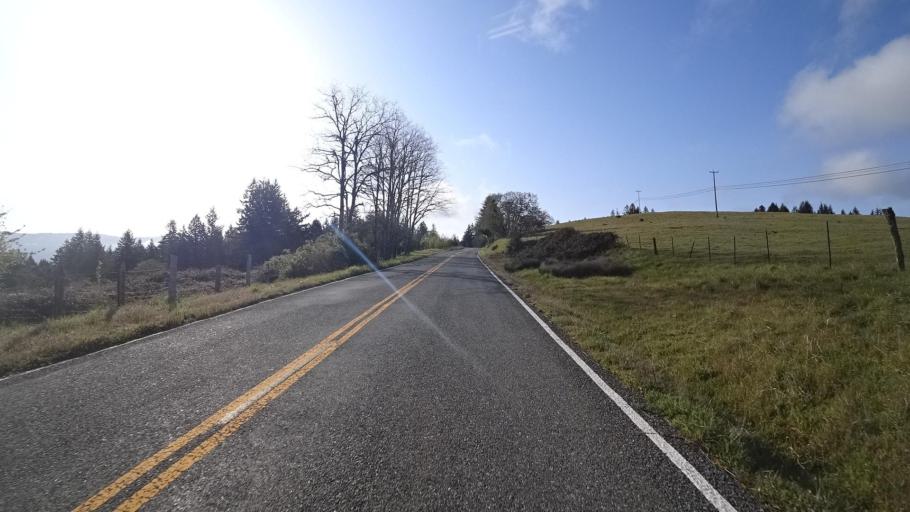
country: US
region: California
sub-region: Humboldt County
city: Blue Lake
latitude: 40.7294
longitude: -123.9473
